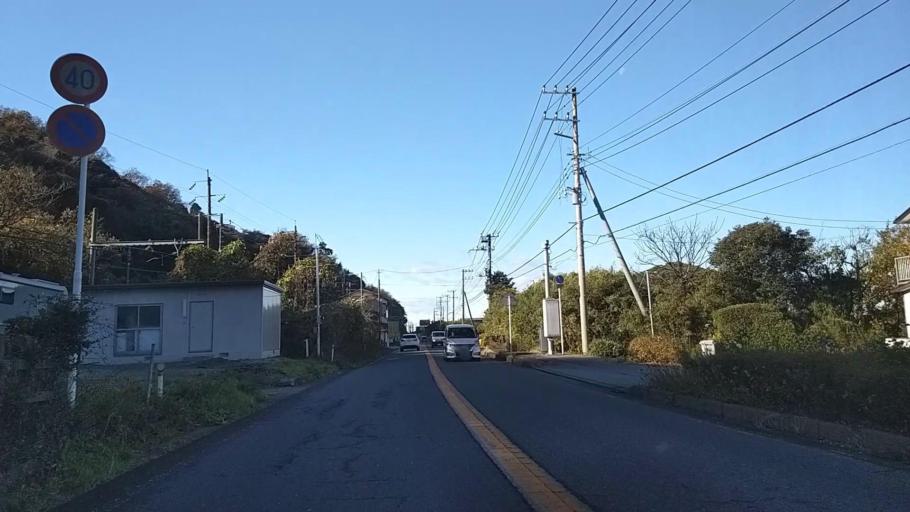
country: JP
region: Chiba
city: Futtsu
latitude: 35.2148
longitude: 139.8575
